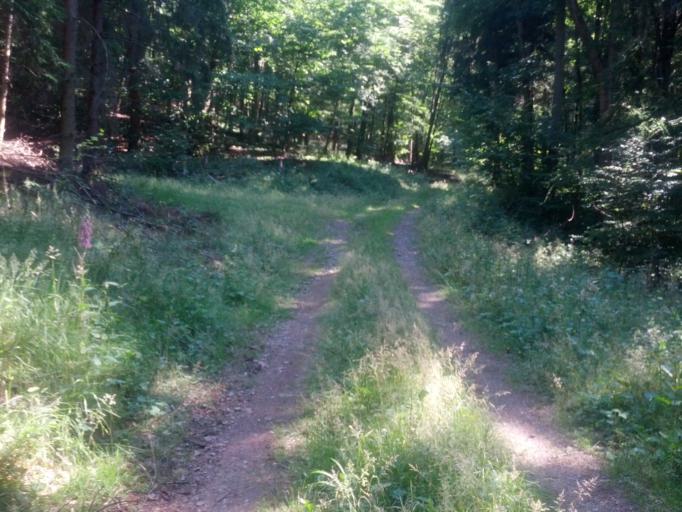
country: DE
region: Thuringia
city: Eisenach
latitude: 50.9715
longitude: 10.2809
